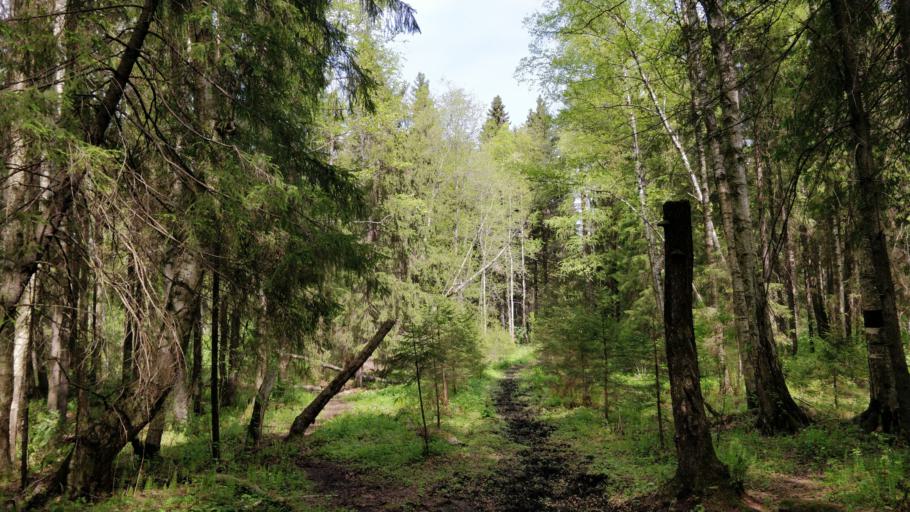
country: RU
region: Perm
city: Kondratovo
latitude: 57.9832
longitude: 56.1497
